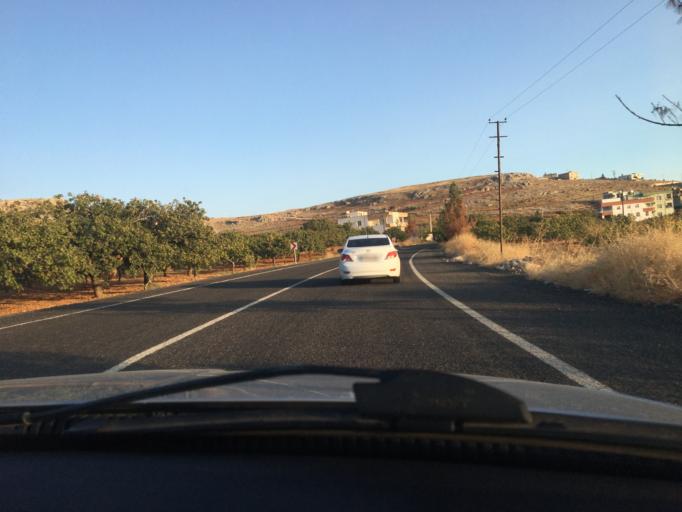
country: TR
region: Sanliurfa
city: Halfeti
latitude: 37.2155
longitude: 37.9614
